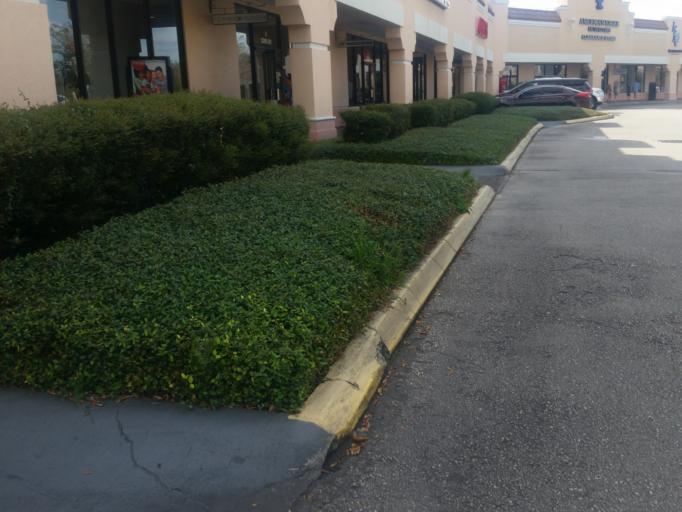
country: US
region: Florida
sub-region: Orange County
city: Tangelo Park
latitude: 28.4673
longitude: -81.4510
